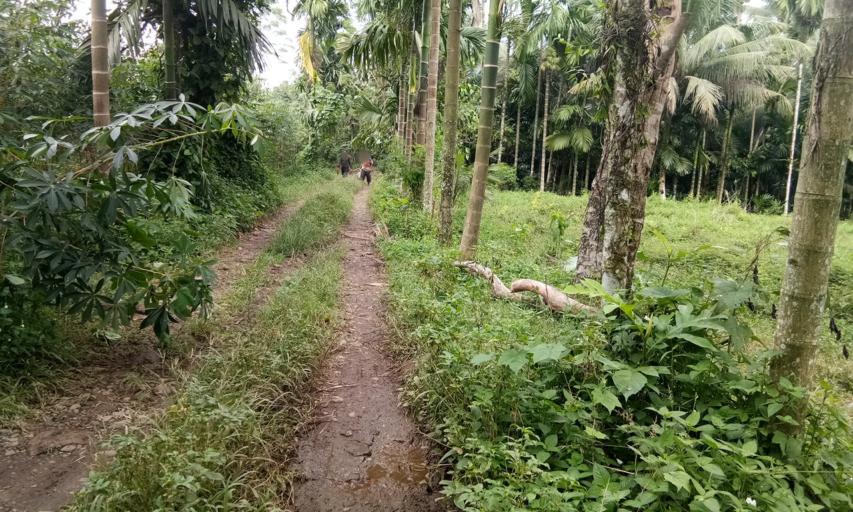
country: ID
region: North Sumatra
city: Deli Tua
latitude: 3.4628
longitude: 98.6098
